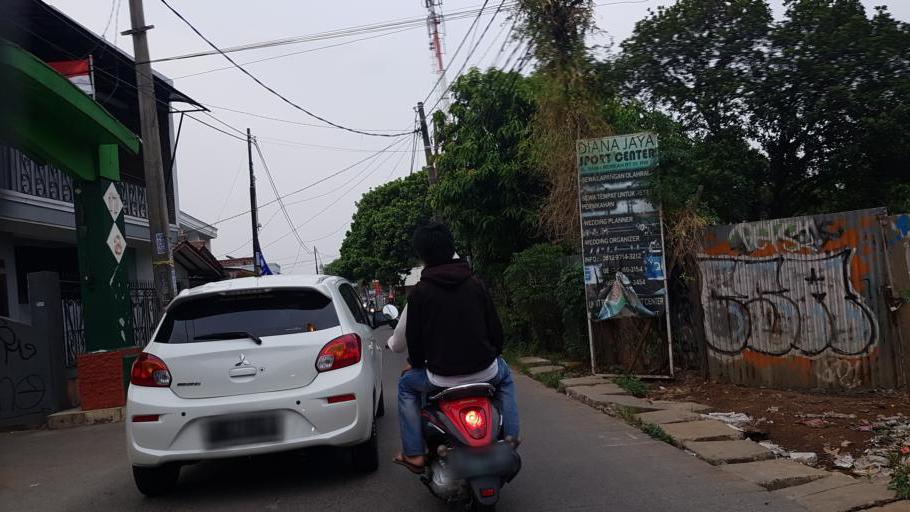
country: ID
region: West Java
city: Depok
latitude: -6.3763
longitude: 106.8014
